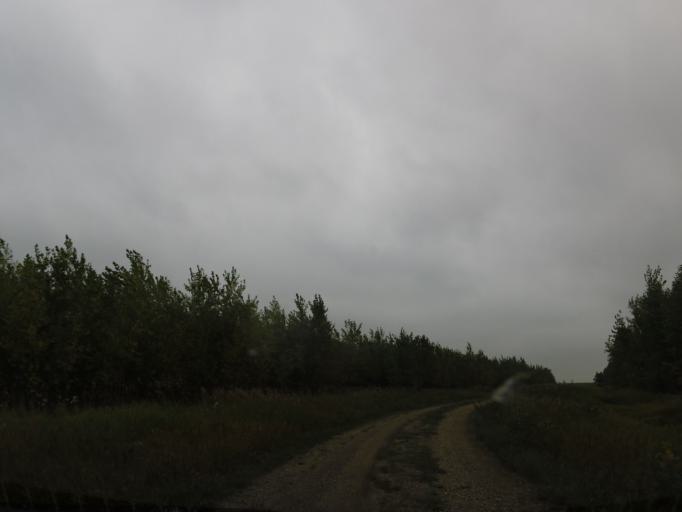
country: US
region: North Dakota
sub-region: Walsh County
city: Grafton
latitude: 48.4273
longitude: -97.1182
